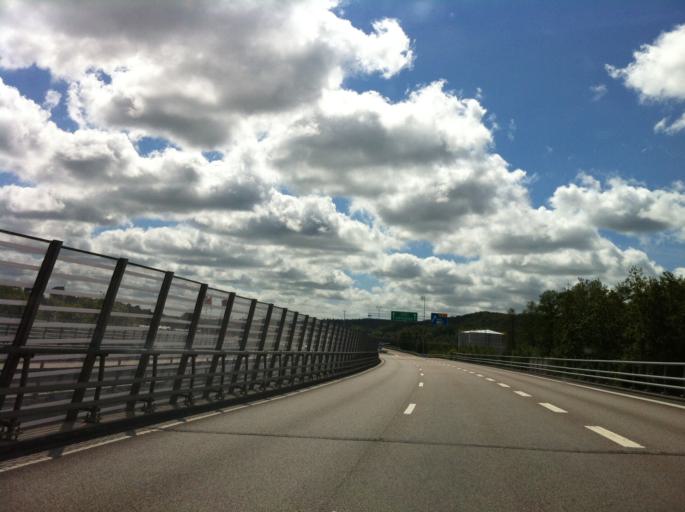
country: SE
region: Vaestra Goetaland
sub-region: Ale Kommun
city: Alafors
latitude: 57.9336
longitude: 12.0888
